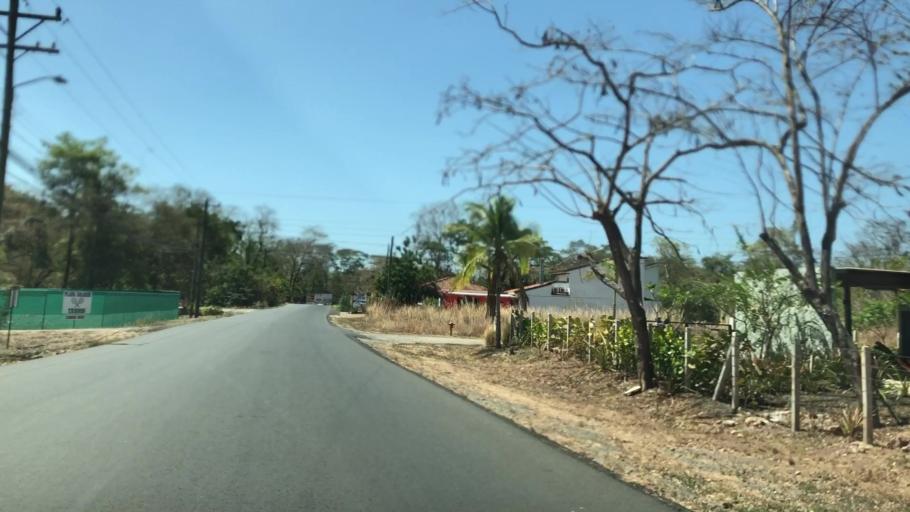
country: CR
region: Guanacaste
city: Belen
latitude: 10.3380
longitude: -85.8460
